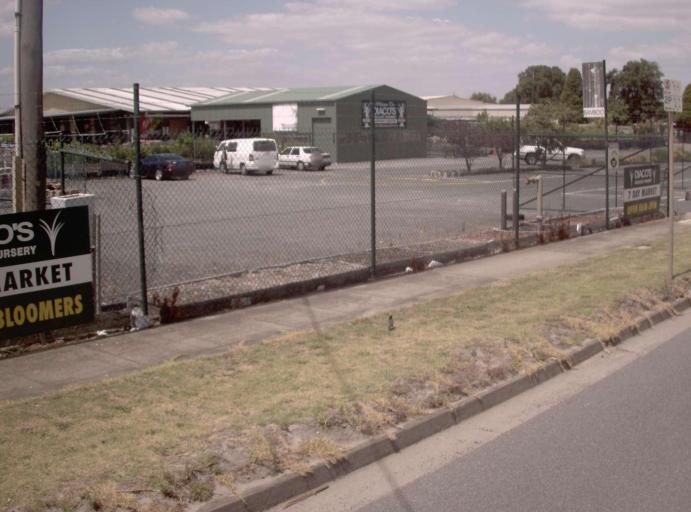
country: AU
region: Victoria
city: Heatherton
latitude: -37.9571
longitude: 145.1006
